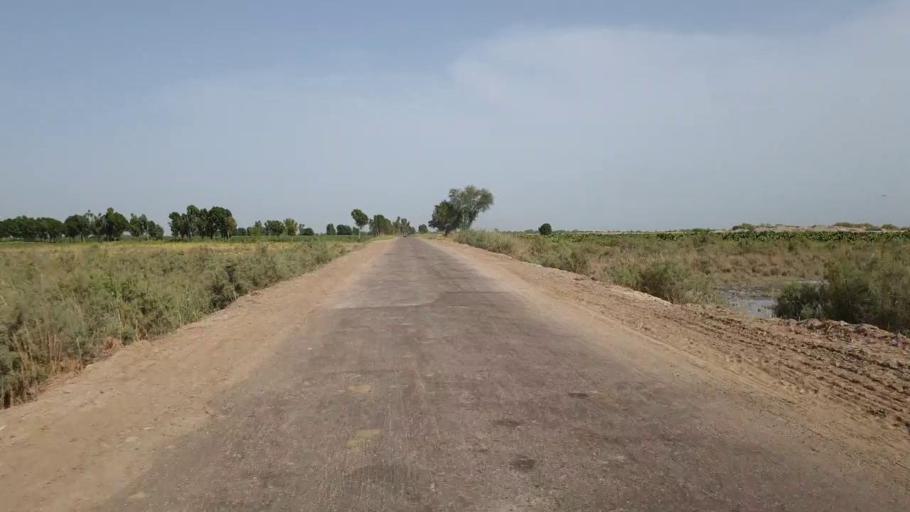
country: PK
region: Sindh
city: Sakrand
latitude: 26.2804
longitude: 68.2681
